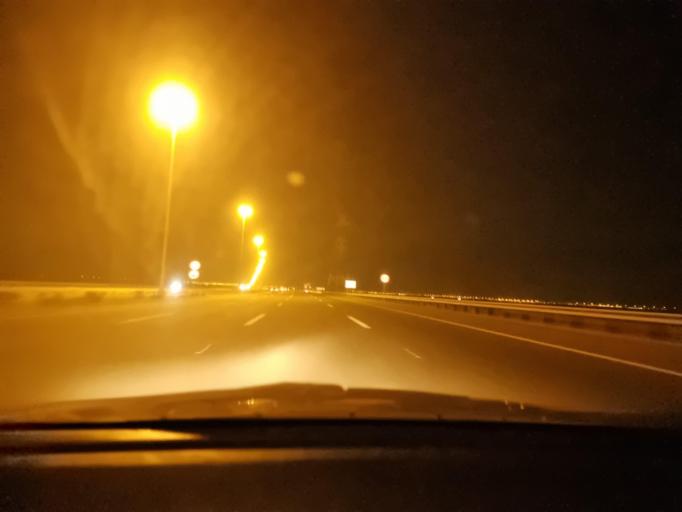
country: AE
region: Dubai
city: Dubai
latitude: 24.7389
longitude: 54.8885
